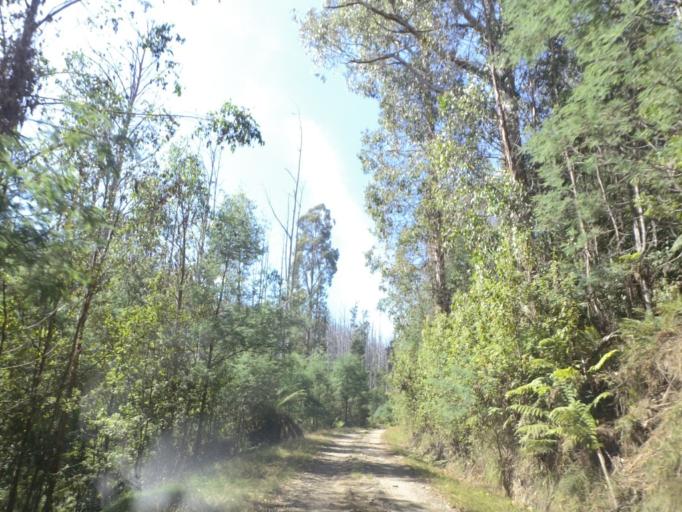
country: AU
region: Victoria
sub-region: Yarra Ranges
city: Millgrove
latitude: -37.5024
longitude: 145.8457
